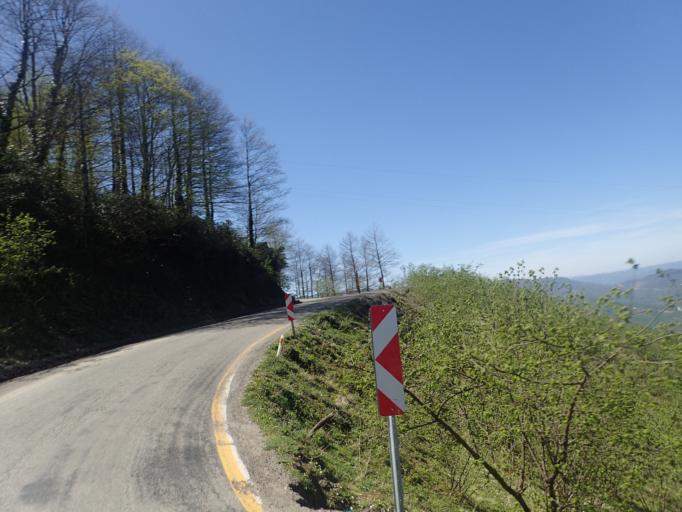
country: TR
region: Ordu
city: Kabaduz
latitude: 40.7964
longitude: 37.9139
